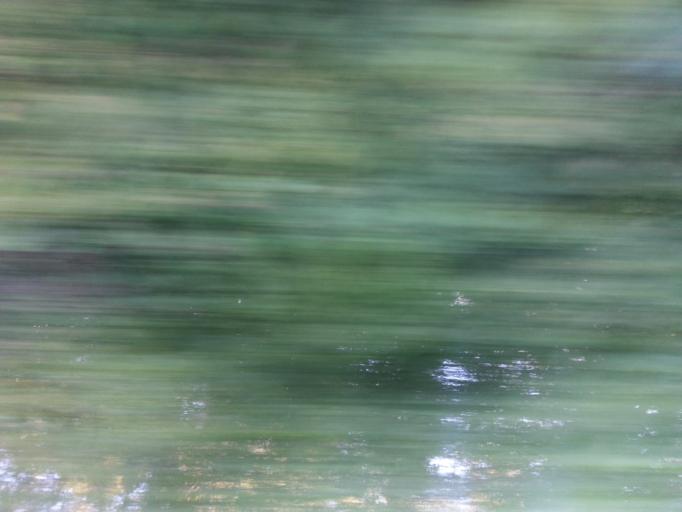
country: US
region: Tennessee
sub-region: Blount County
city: Alcoa
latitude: 35.8323
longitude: -83.9797
